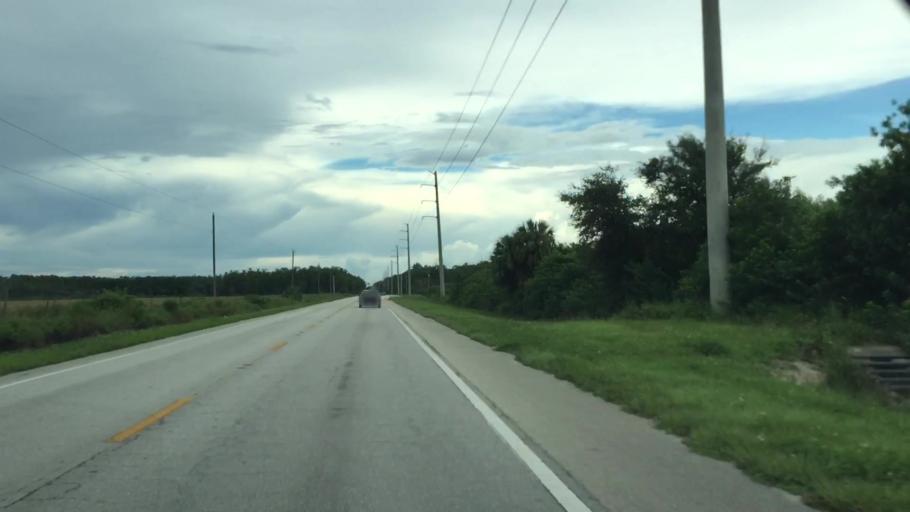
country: US
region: Florida
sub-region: Collier County
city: Orangetree
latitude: 26.3233
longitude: -81.5951
